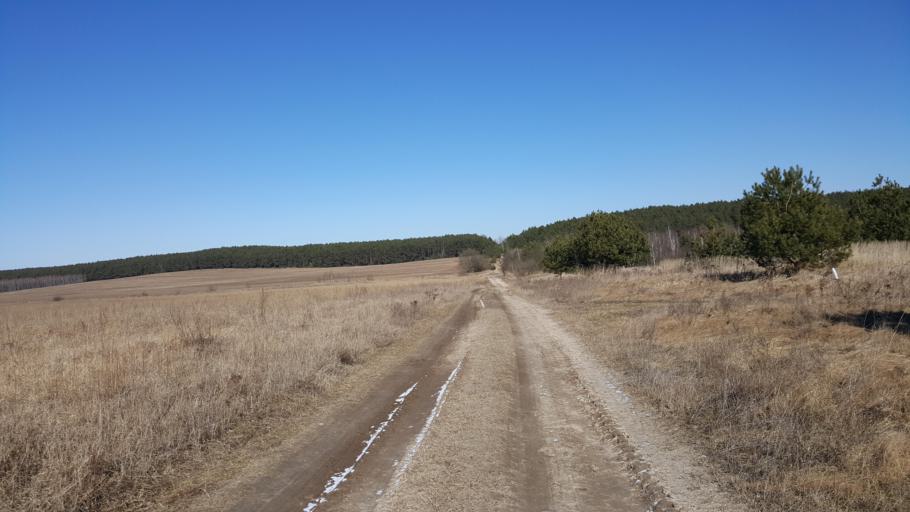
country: BY
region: Brest
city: Kamyanyets
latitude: 52.3742
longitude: 23.8366
